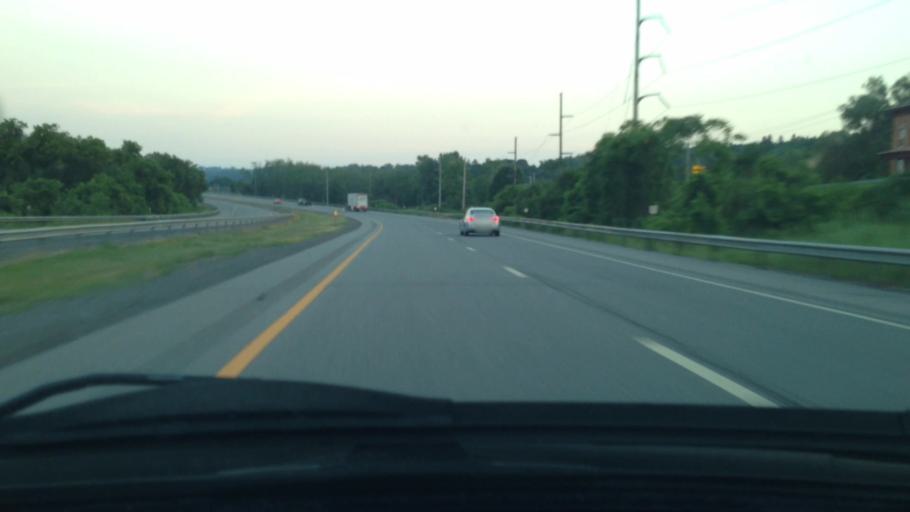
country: US
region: New York
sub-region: Montgomery County
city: Fort Plain
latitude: 42.9435
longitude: -74.6297
